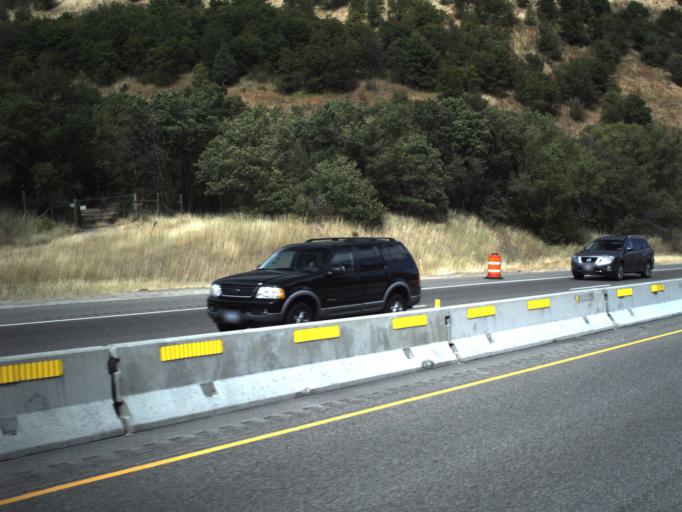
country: US
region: Utah
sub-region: Cache County
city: Wellsville
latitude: 41.6038
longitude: -111.9770
